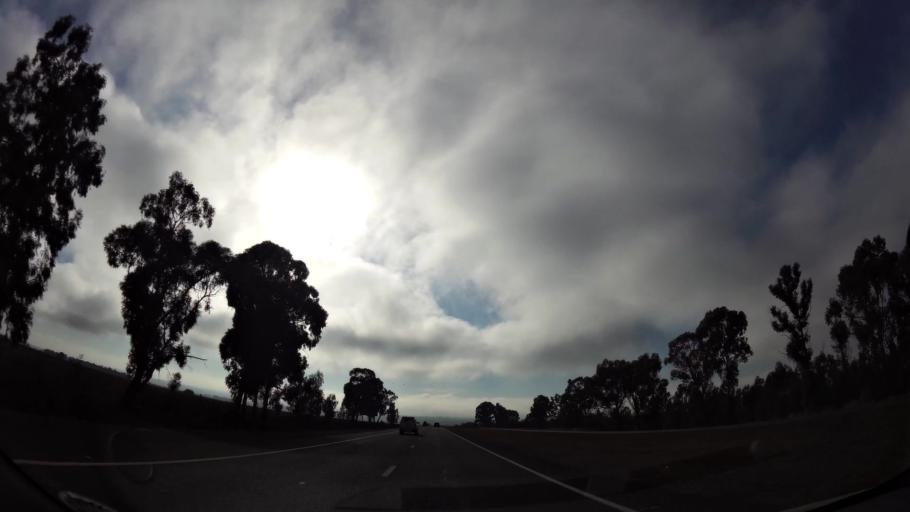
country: ZA
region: Mpumalanga
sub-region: Nkangala District Municipality
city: Delmas
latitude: -26.0386
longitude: 28.8475
